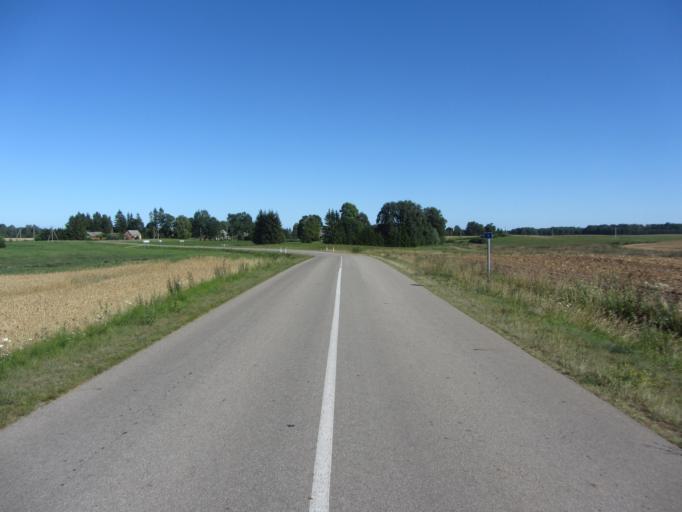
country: LT
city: Obeliai
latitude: 55.8165
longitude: 25.1240
